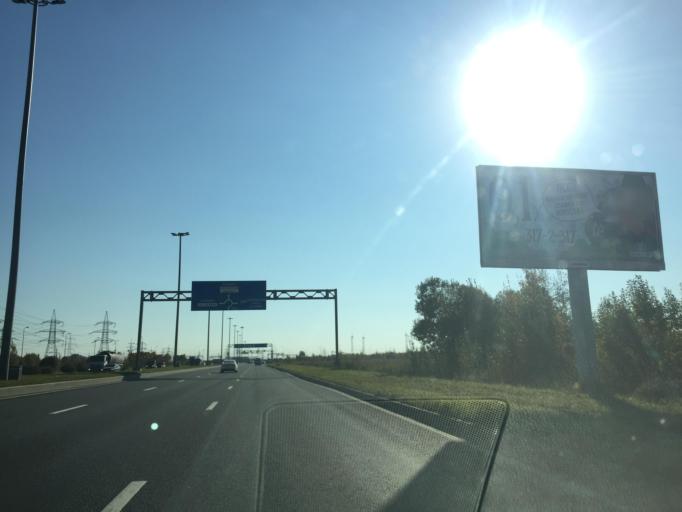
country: RU
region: St.-Petersburg
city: Petro-Slavyanka
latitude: 59.7521
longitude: 30.5253
